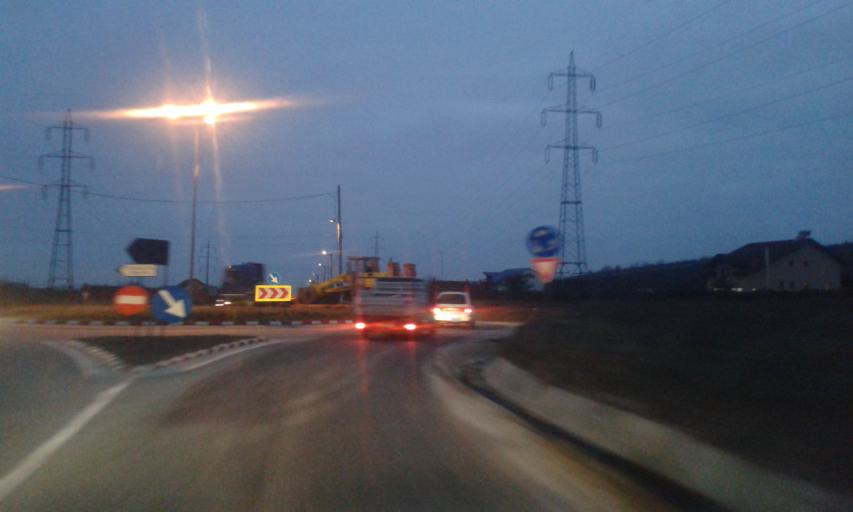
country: RO
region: Gorj
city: Targu Jiu
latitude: 45.0527
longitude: 23.2619
